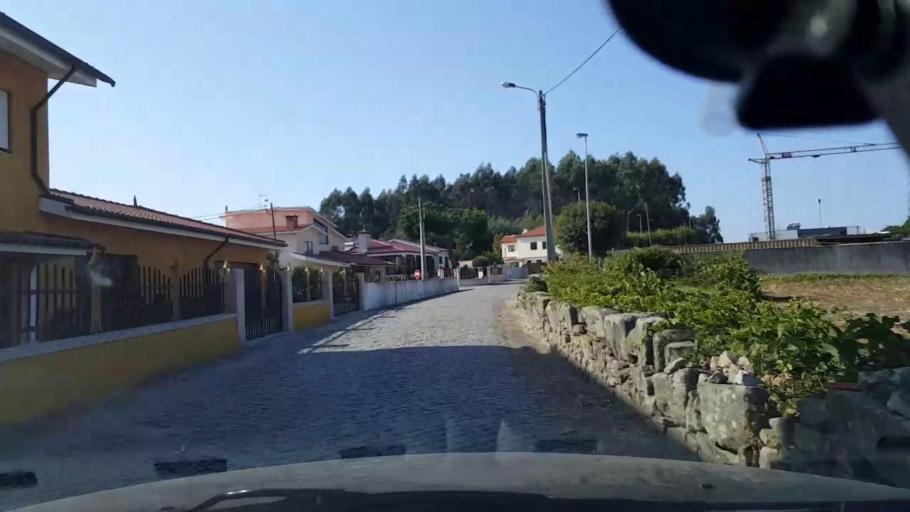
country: PT
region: Porto
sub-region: Vila do Conde
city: Arvore
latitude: 41.3543
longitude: -8.7066
